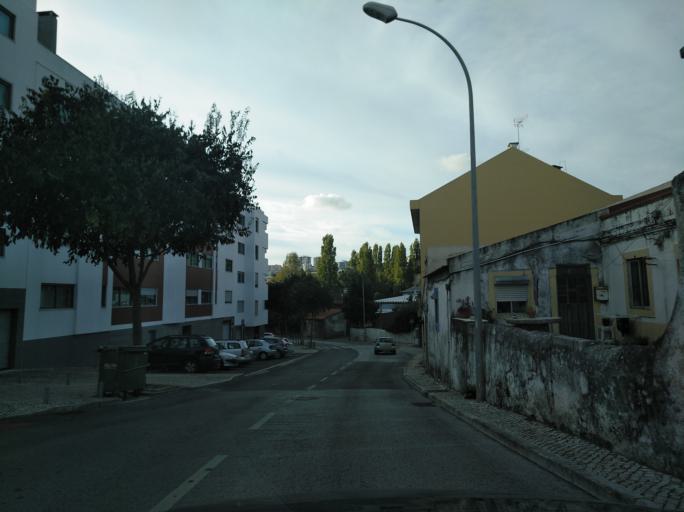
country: PT
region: Lisbon
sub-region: Oeiras
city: Alges
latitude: 38.7218
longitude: -9.2226
